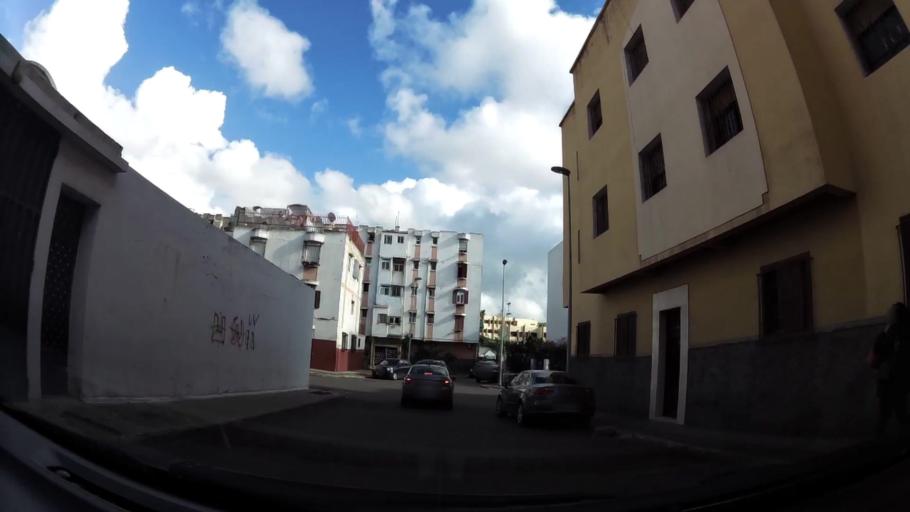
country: MA
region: Grand Casablanca
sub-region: Casablanca
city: Casablanca
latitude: 33.5413
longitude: -7.5968
